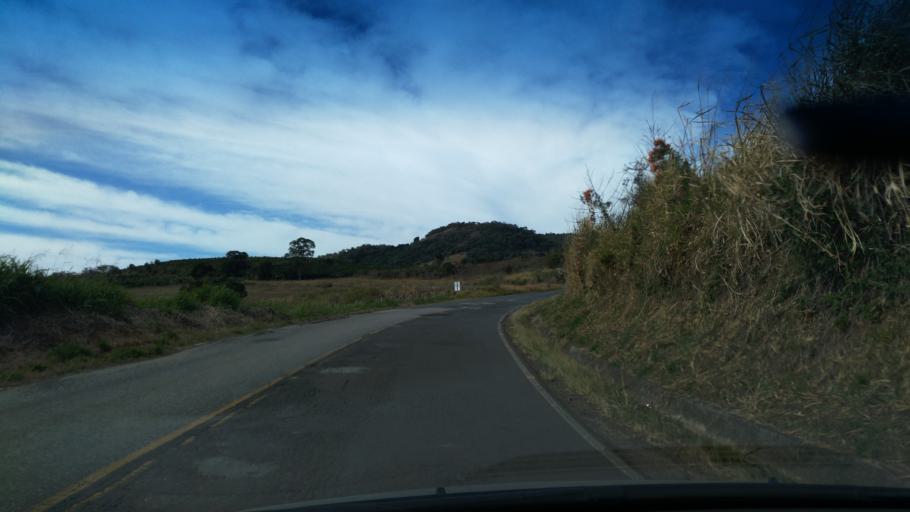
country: BR
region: Minas Gerais
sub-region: Andradas
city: Andradas
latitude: -22.0591
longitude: -46.3927
